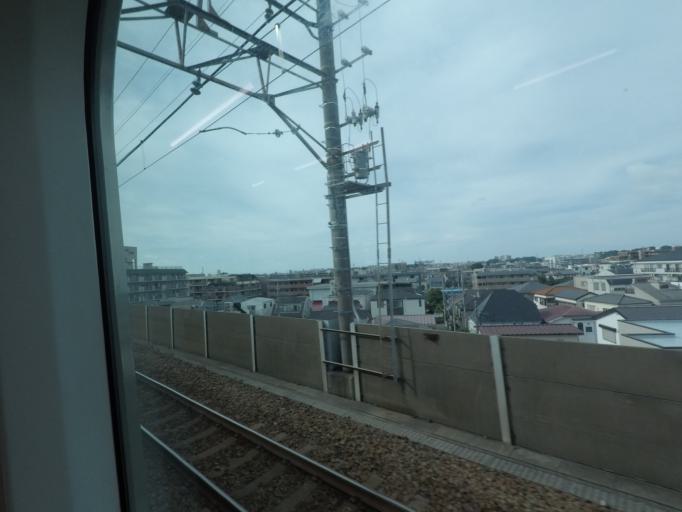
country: JP
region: Kanagawa
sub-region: Kawasaki-shi
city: Kawasaki
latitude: 35.5785
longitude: 139.6462
